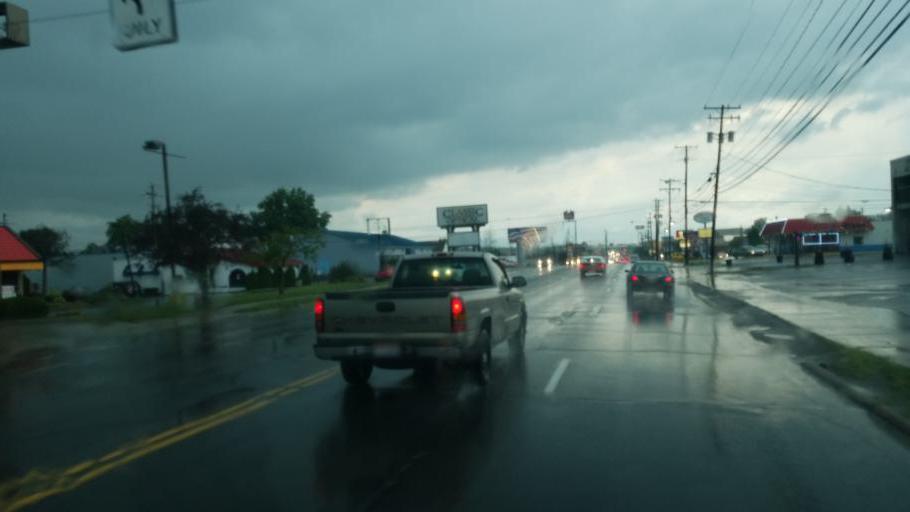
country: US
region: Ohio
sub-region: Trumbull County
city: Churchill
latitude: 41.1492
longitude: -80.6651
